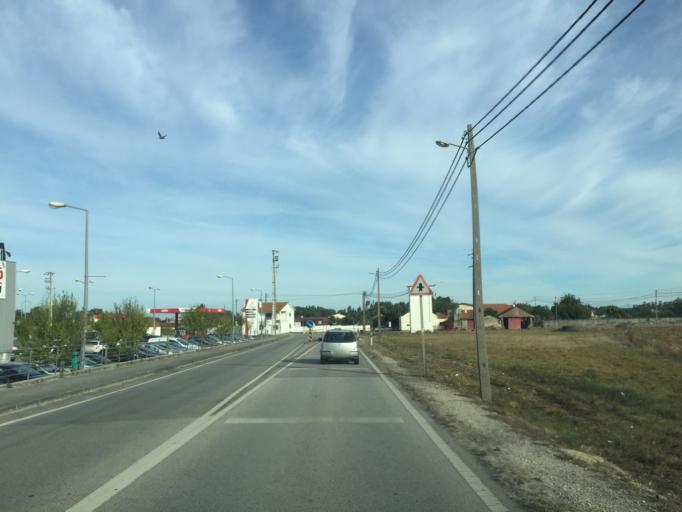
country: PT
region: Leiria
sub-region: Pombal
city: Lourical
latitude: 39.9681
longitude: -8.7922
